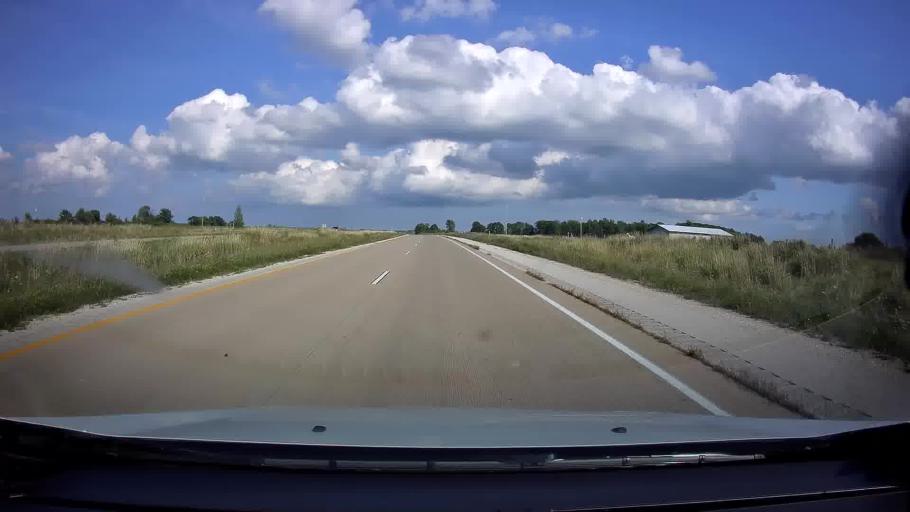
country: US
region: Wisconsin
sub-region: Kewaunee County
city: Luxemburg
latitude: 44.7165
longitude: -87.6635
